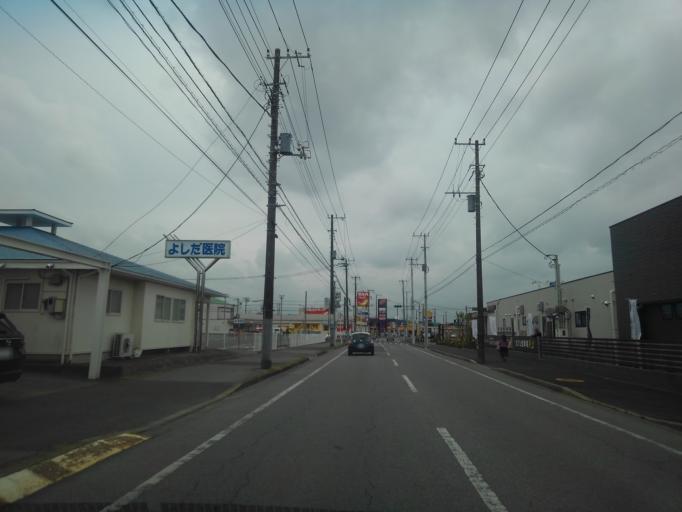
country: JP
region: Chiba
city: Kimitsu
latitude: 35.3269
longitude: 139.9211
